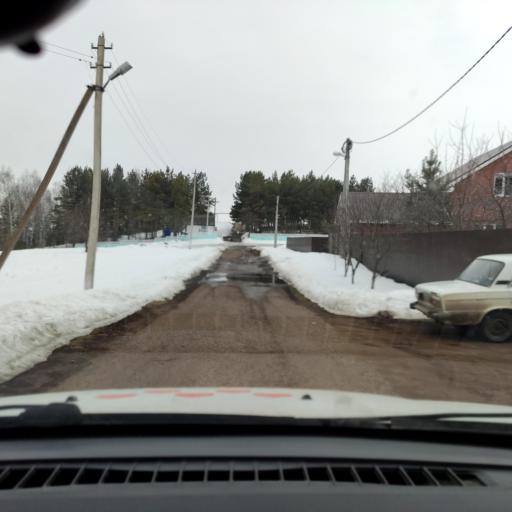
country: RU
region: Bashkortostan
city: Kushnarenkovo
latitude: 55.1187
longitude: 55.3561
